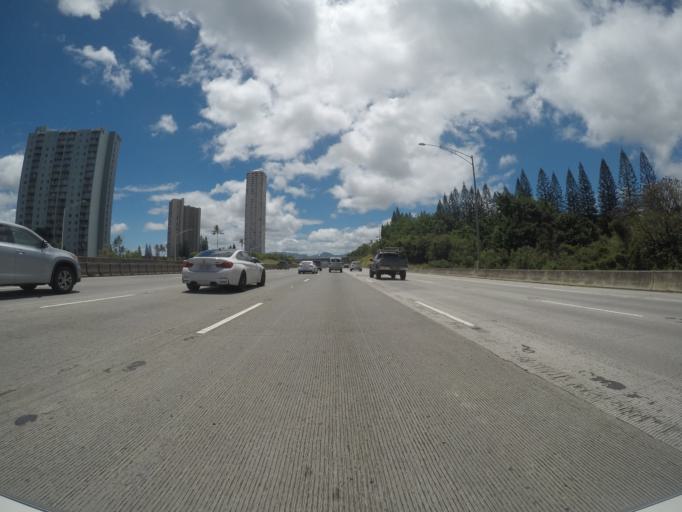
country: US
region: Hawaii
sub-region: Honolulu County
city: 'Aiea
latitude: 21.3877
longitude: -157.9382
